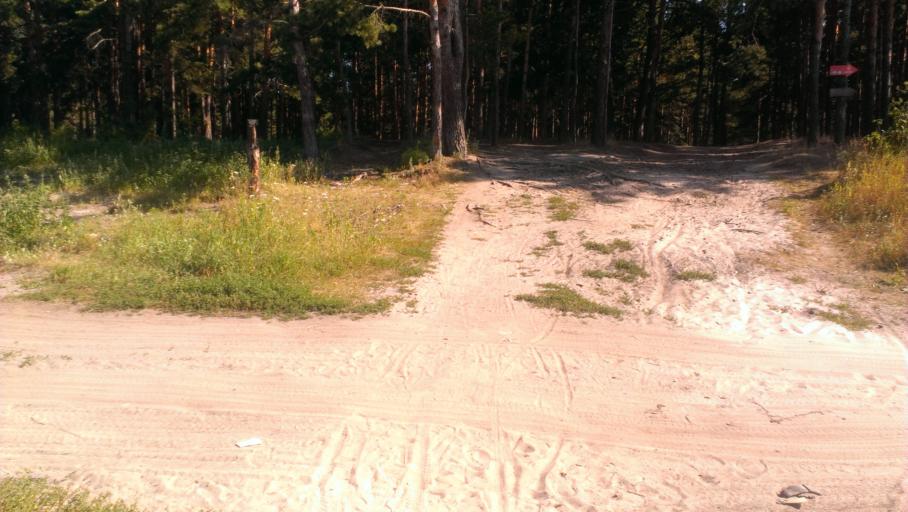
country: RU
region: Altai Krai
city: Novosilikatnyy
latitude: 53.3198
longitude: 83.6852
